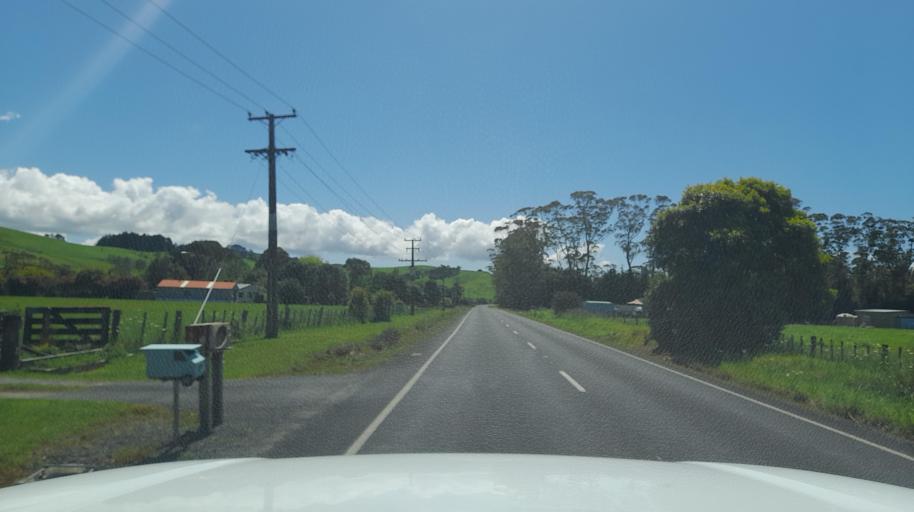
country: NZ
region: Northland
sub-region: Far North District
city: Taipa
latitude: -35.0287
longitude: 173.4813
